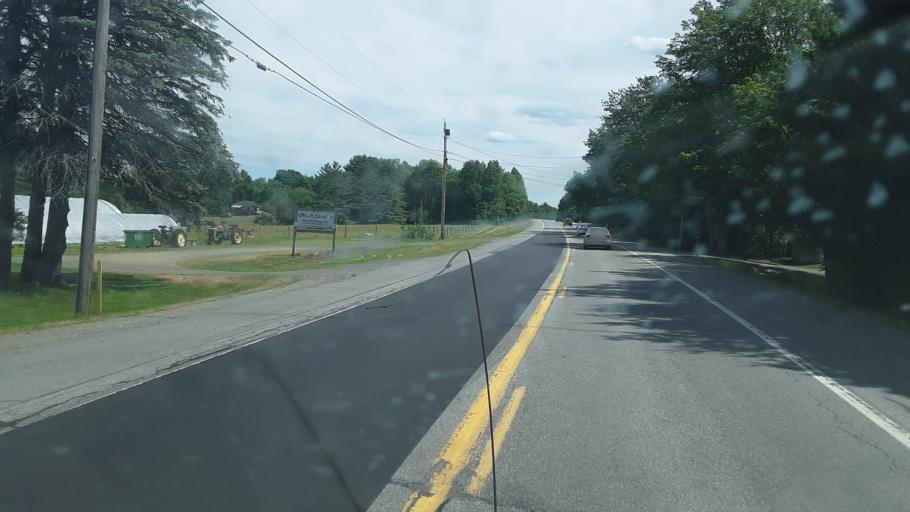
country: US
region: Maine
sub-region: Somerset County
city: Norridgewock
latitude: 44.6519
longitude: -69.6983
